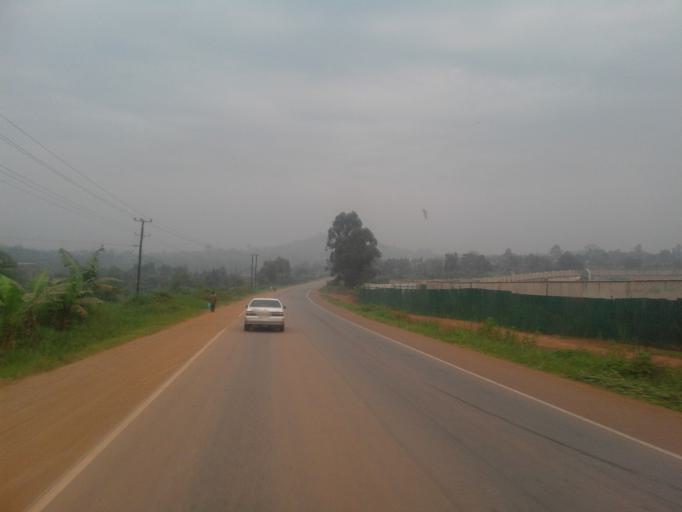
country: UG
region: Central Region
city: Lugazi
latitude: 0.3889
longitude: 32.8526
